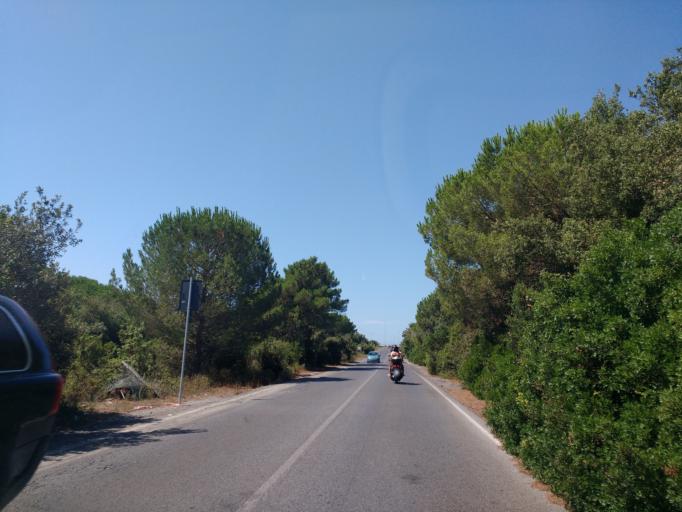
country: IT
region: Latium
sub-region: Citta metropolitana di Roma Capitale
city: Acilia-Castel Fusano-Ostia Antica
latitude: 41.7043
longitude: 12.3495
